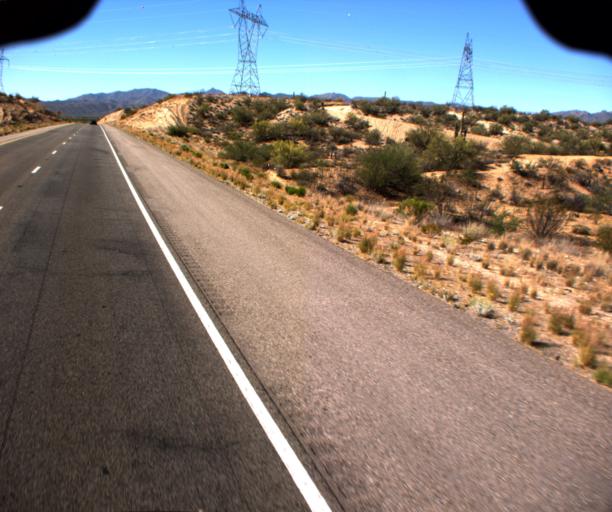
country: US
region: Arizona
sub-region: Yavapai County
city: Bagdad
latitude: 34.7520
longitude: -113.6164
